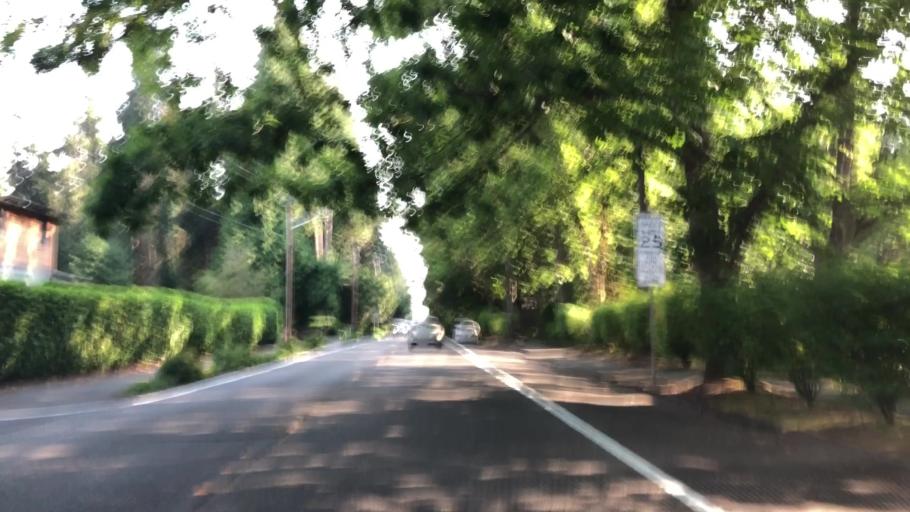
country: US
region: Washington
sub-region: King County
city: Newport
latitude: 47.5875
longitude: -122.1966
